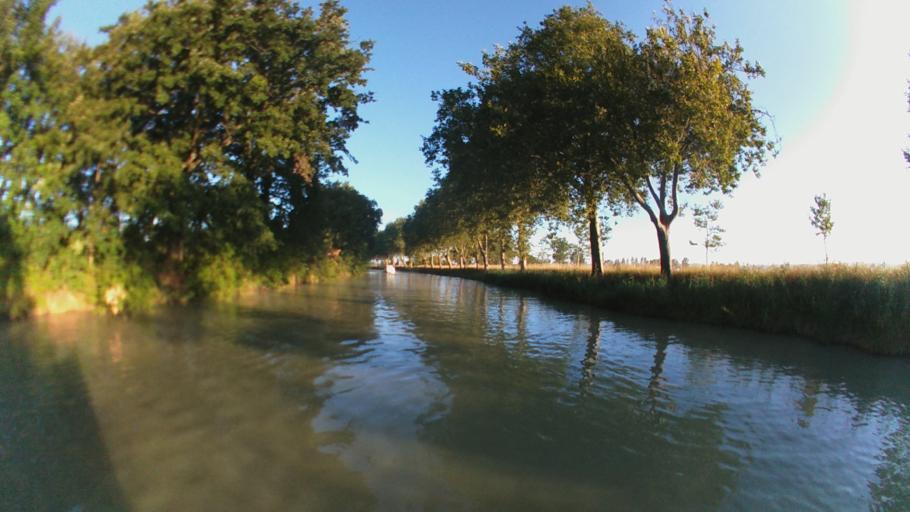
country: FR
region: Midi-Pyrenees
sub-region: Departement de la Haute-Garonne
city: Villenouvelle
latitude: 43.4111
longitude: 1.6616
